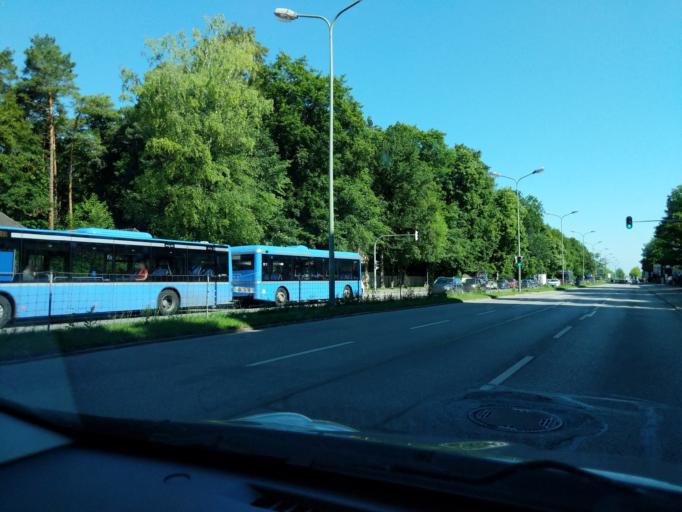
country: DE
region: Bavaria
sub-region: Upper Bavaria
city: Neuried
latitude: 48.1086
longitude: 11.5024
